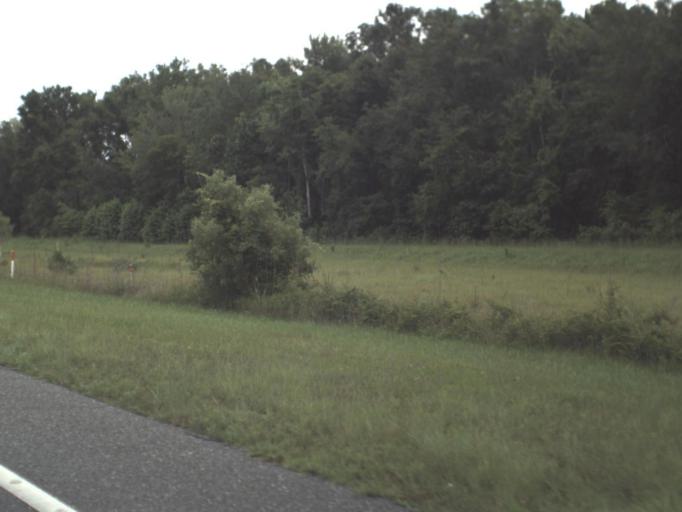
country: US
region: Florida
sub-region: Levy County
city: Bronson
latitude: 29.3257
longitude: -82.7674
